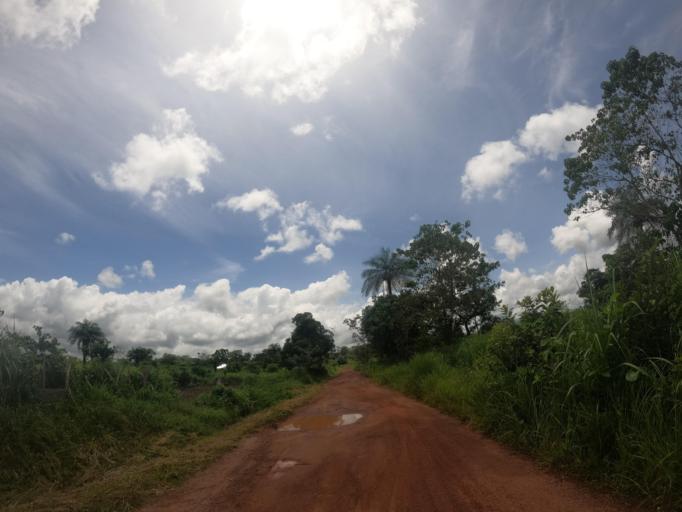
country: SL
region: Northern Province
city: Makeni
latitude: 9.1305
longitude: -12.2436
